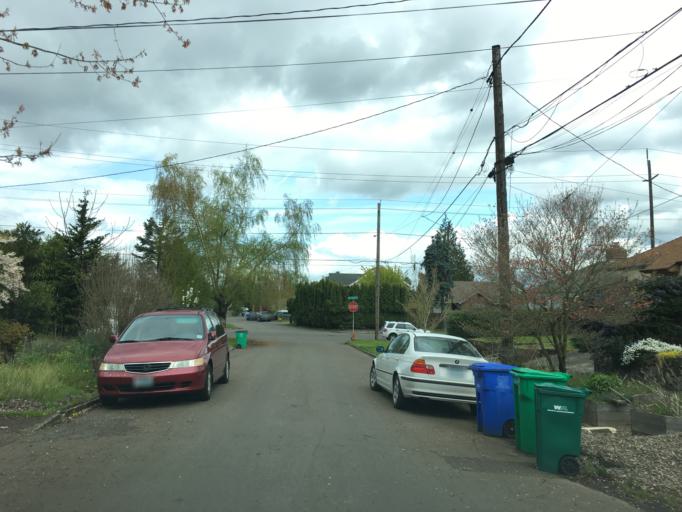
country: US
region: Oregon
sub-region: Multnomah County
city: Lents
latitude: 45.5548
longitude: -122.5847
